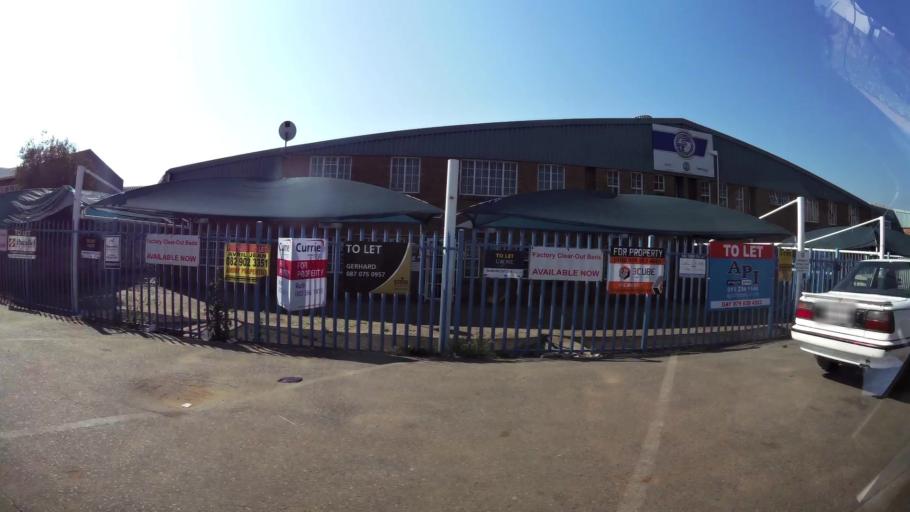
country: ZA
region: Gauteng
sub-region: Ekurhuleni Metropolitan Municipality
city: Boksburg
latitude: -26.1705
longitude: 28.2277
